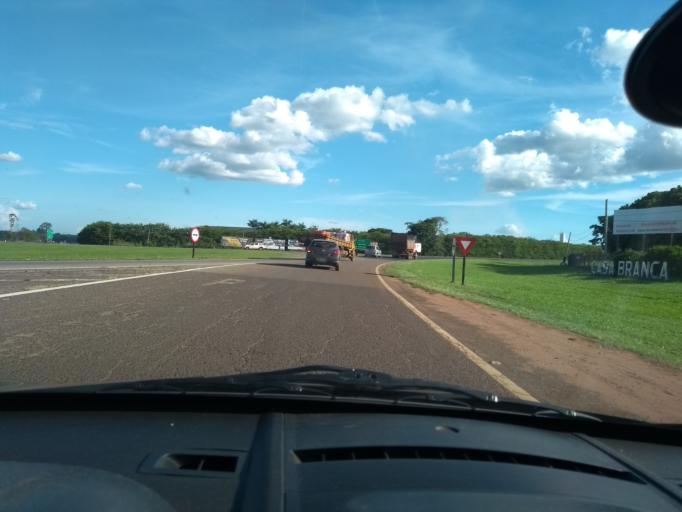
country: BR
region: Sao Paulo
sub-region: Casa Branca
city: Casa Branca
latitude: -21.7858
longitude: -47.0659
